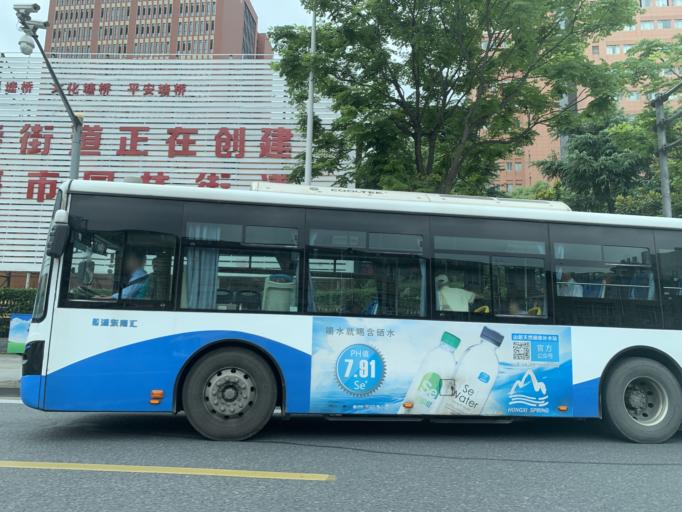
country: CN
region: Shanghai Shi
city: Huamu
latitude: 31.2100
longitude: 121.5198
